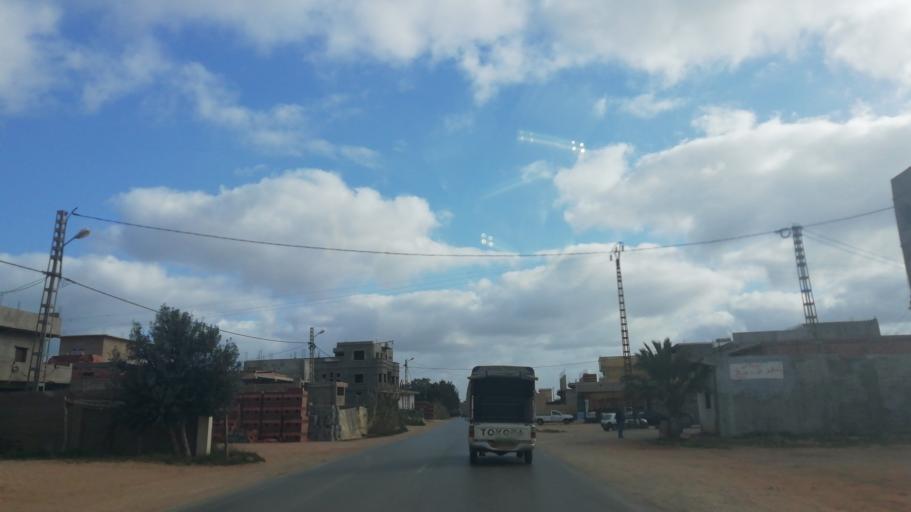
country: DZ
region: Relizane
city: Mazouna
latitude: 36.2653
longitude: 0.6234
